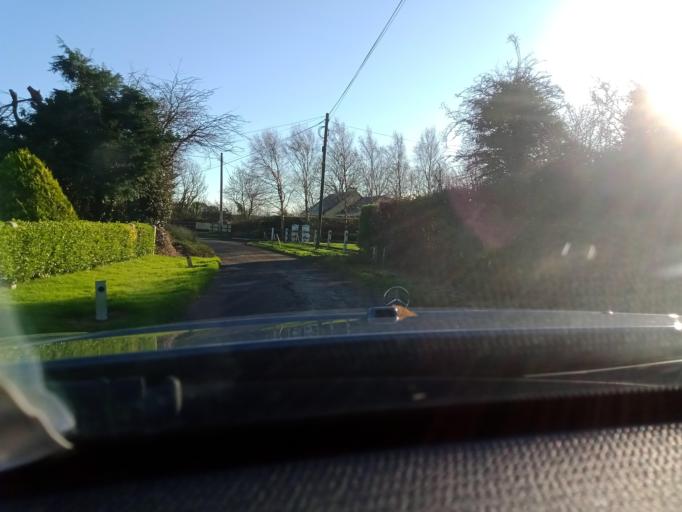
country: IE
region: Leinster
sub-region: Kilkenny
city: Mooncoin
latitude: 52.2955
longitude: -7.1866
